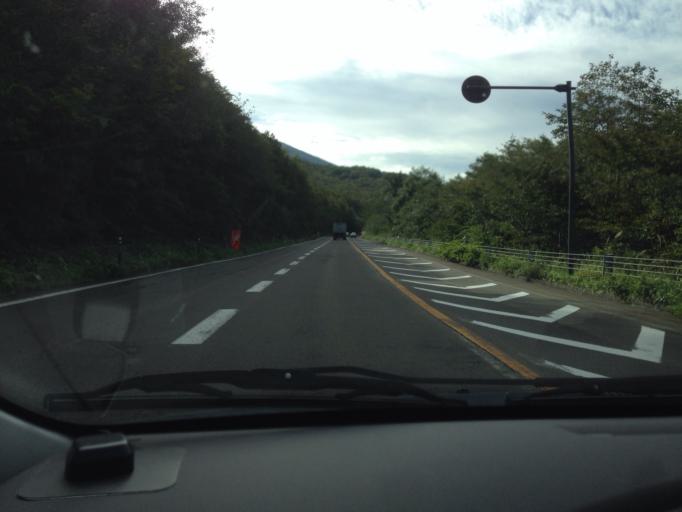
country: JP
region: Fukushima
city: Nihommatsu
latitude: 37.6500
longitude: 140.3292
